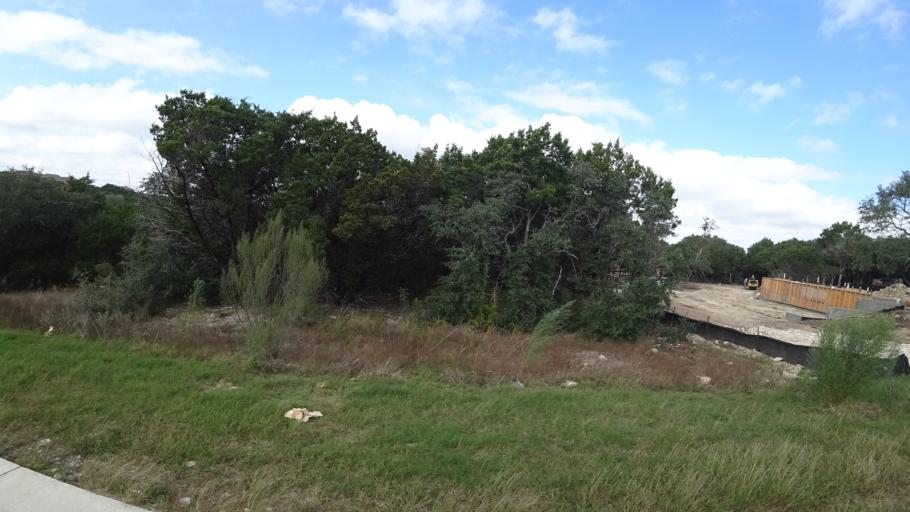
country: US
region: Texas
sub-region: Travis County
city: Bee Cave
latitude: 30.2542
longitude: -97.9267
